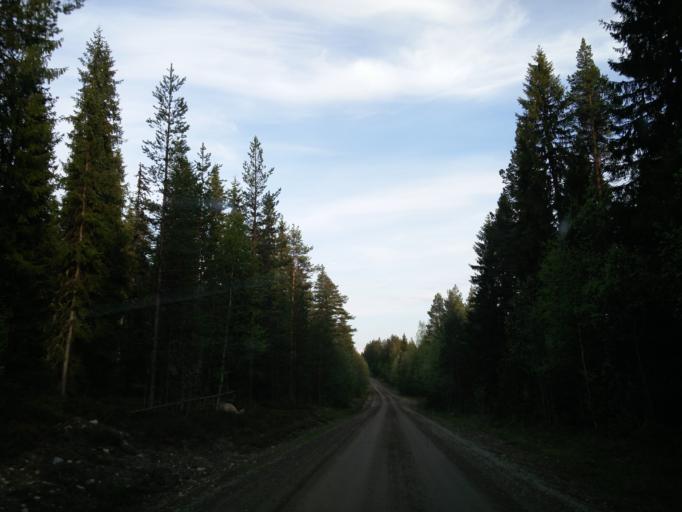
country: SE
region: Jaemtland
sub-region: Bergs Kommun
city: Hoverberg
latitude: 62.5519
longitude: 14.3955
